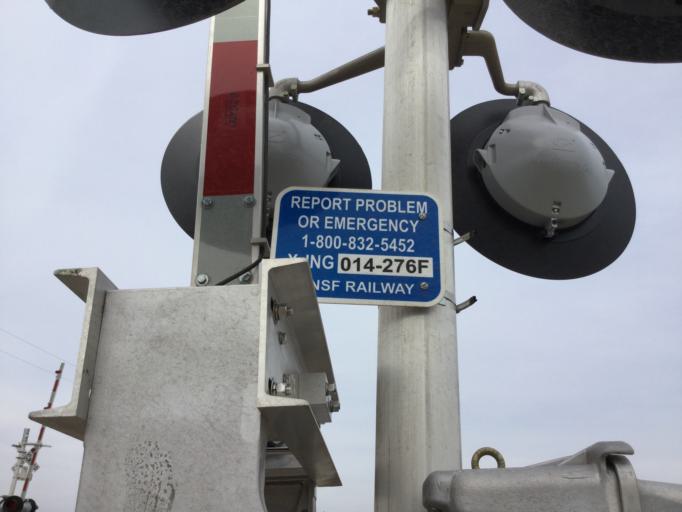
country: US
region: Kansas
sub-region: Barber County
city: Kiowa
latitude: 37.1266
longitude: -98.3661
